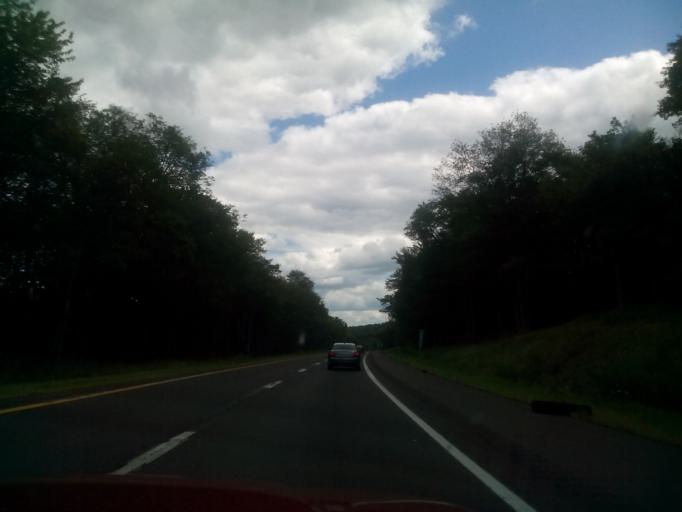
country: US
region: Pennsylvania
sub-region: Carbon County
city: Towamensing Trails
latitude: 41.0825
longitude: -75.6219
